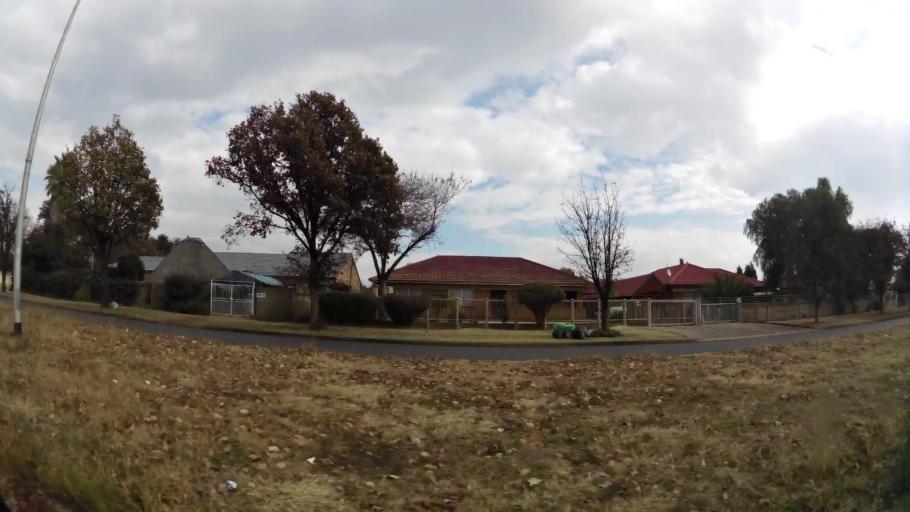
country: ZA
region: Gauteng
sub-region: Sedibeng District Municipality
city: Vanderbijlpark
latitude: -26.7239
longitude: 27.8628
